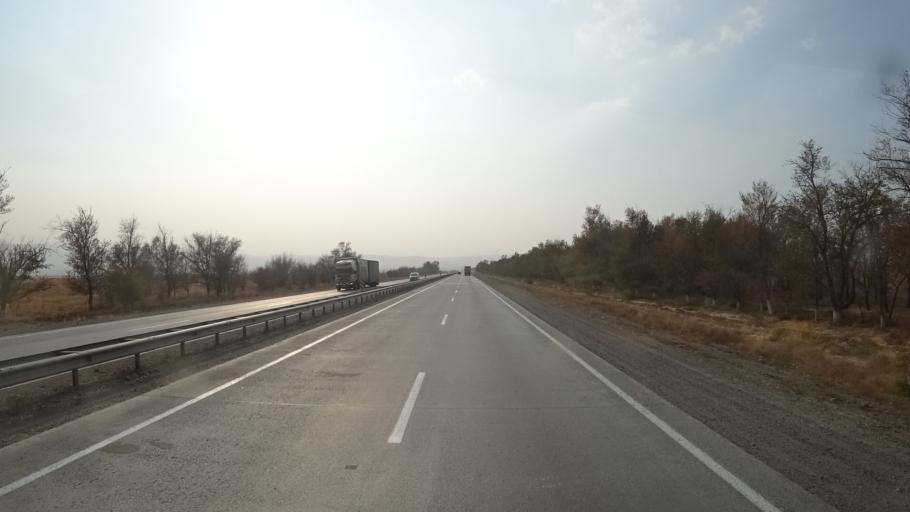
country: KZ
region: Zhambyl
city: Taraz
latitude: 42.7996
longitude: 71.0937
